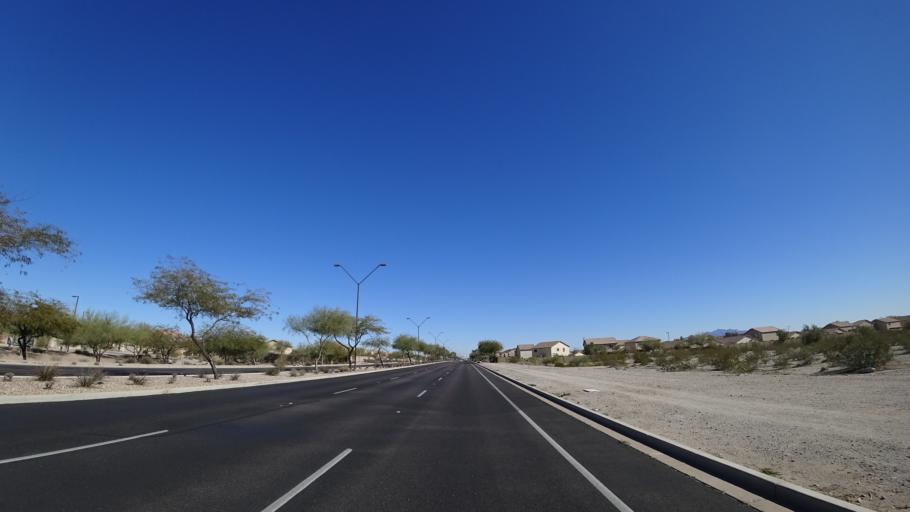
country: US
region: Arizona
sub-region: Maricopa County
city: Buckeye
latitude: 33.4356
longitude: -112.5318
